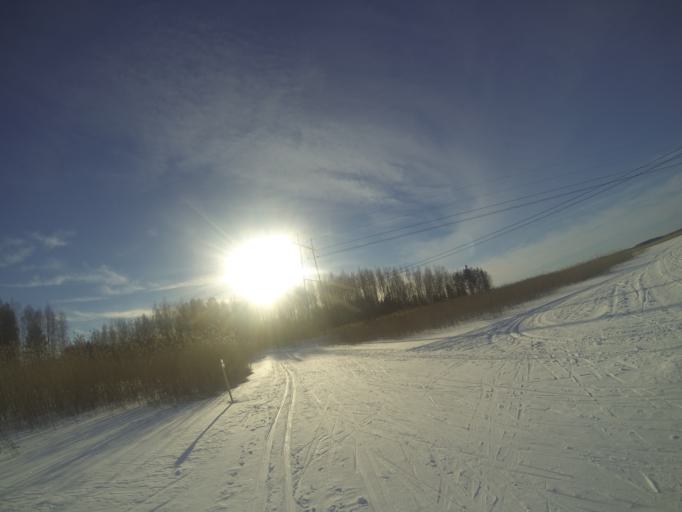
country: FI
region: Southern Savonia
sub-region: Savonlinna
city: Savonlinna
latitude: 61.8956
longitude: 28.9166
